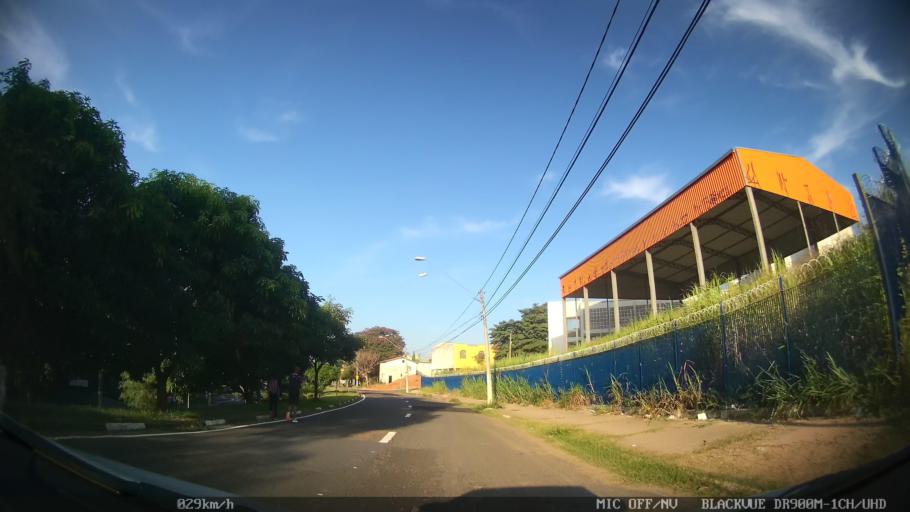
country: BR
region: Sao Paulo
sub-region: Campinas
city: Campinas
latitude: -22.9817
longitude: -47.1188
